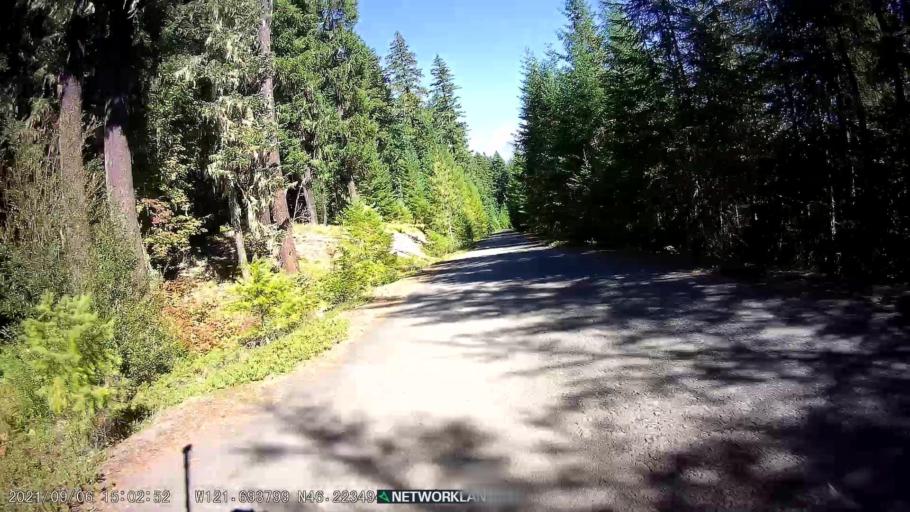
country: US
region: Washington
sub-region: Skamania County
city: Carson
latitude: 46.2231
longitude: -121.6940
